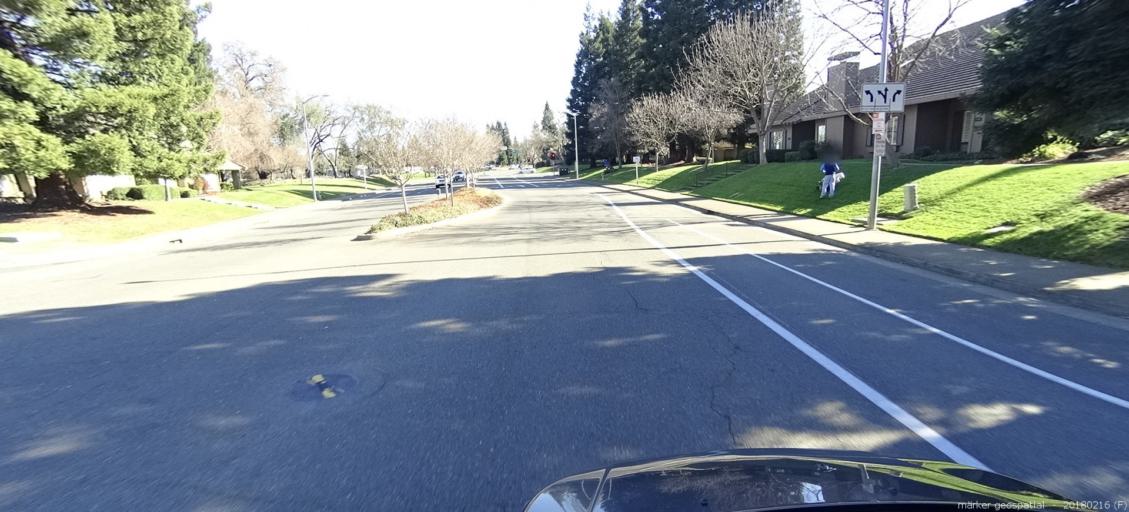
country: US
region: California
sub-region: Sacramento County
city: Gold River
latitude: 38.6246
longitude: -121.2511
